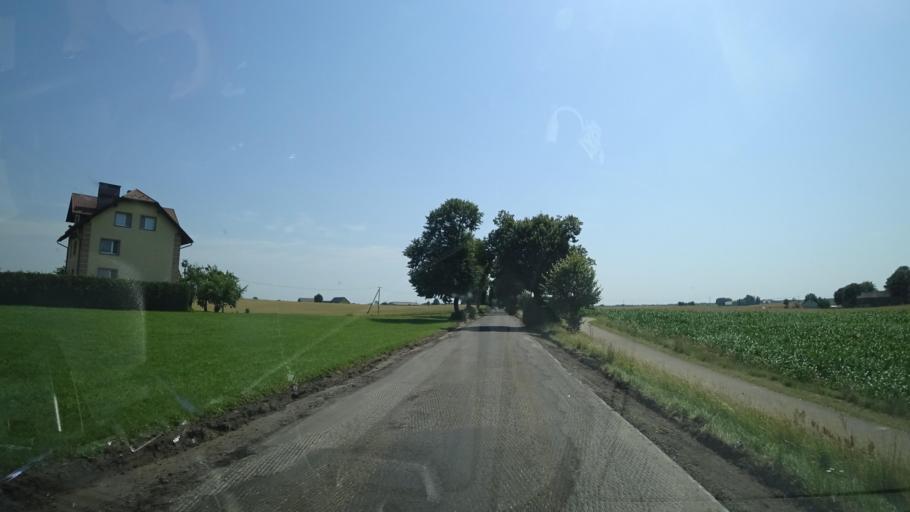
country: PL
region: Pomeranian Voivodeship
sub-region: Powiat chojnicki
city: Brusy
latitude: 53.8740
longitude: 17.6612
